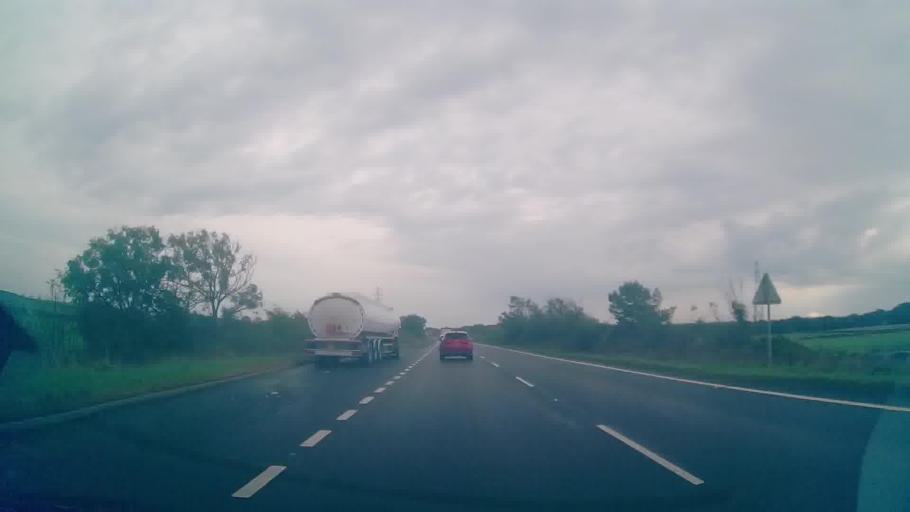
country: GB
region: Scotland
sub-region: Dumfries and Galloway
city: Annan
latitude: 54.9978
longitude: -3.2942
